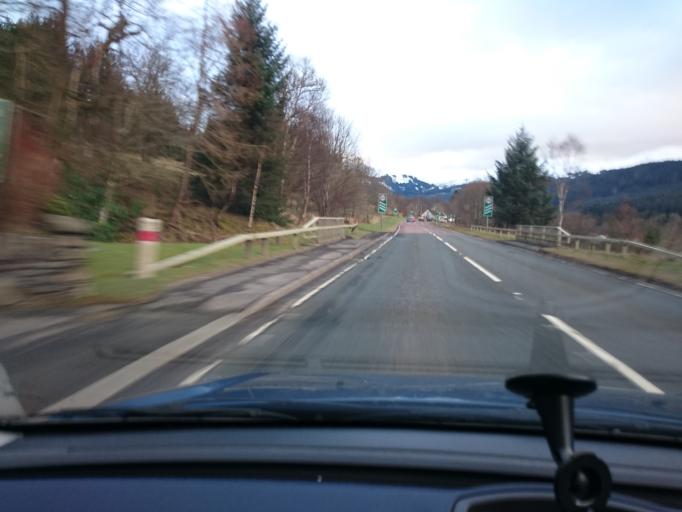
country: GB
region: Scotland
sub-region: Stirling
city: Callander
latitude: 56.3310
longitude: -4.3247
